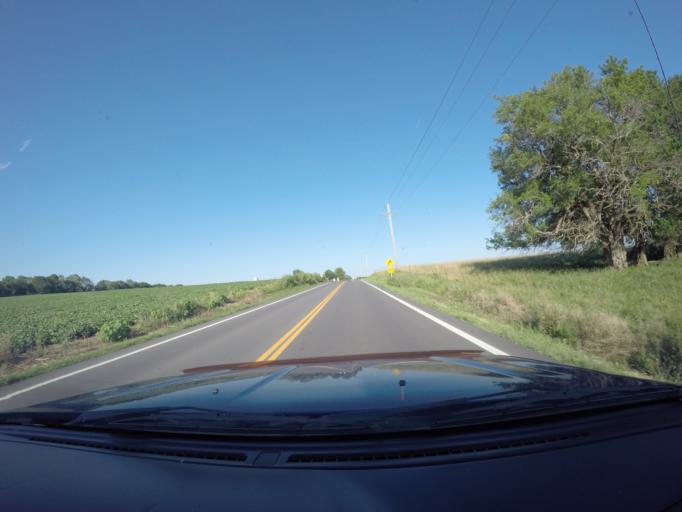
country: US
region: Kansas
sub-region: Douglas County
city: Lawrence
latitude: 39.0657
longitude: -95.3030
